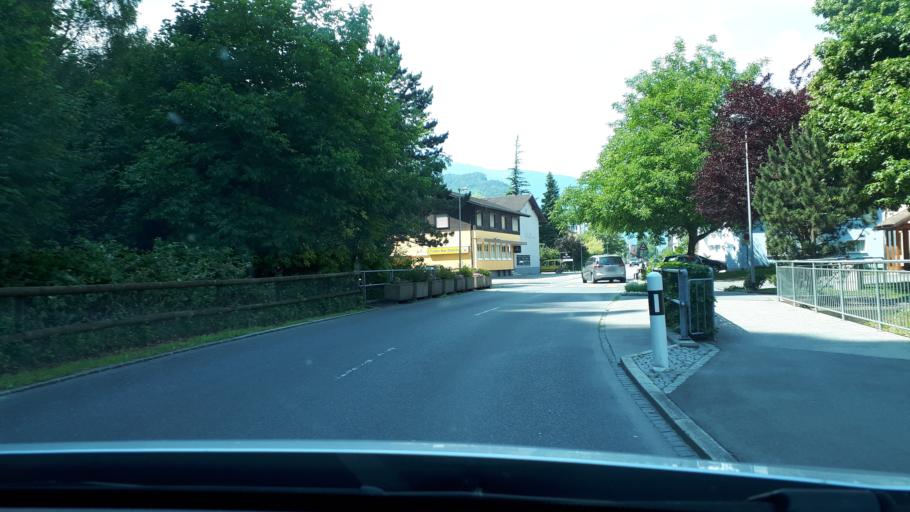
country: LI
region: Balzers
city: Balzers
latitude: 47.0655
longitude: 9.4990
